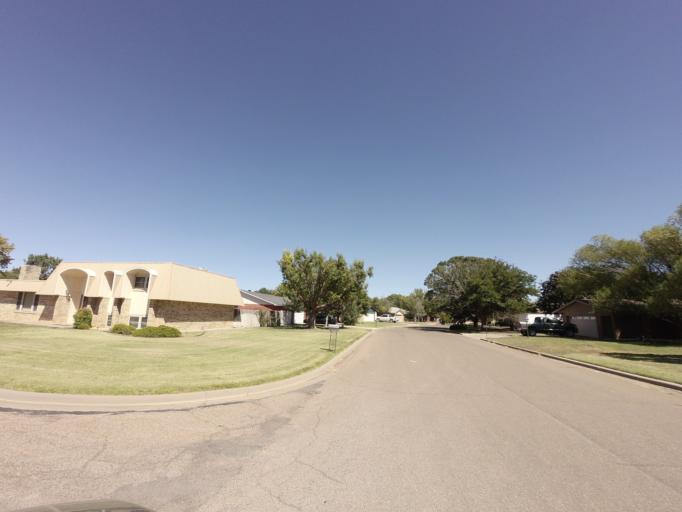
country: US
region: New Mexico
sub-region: Curry County
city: Clovis
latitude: 34.4377
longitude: -103.1812
